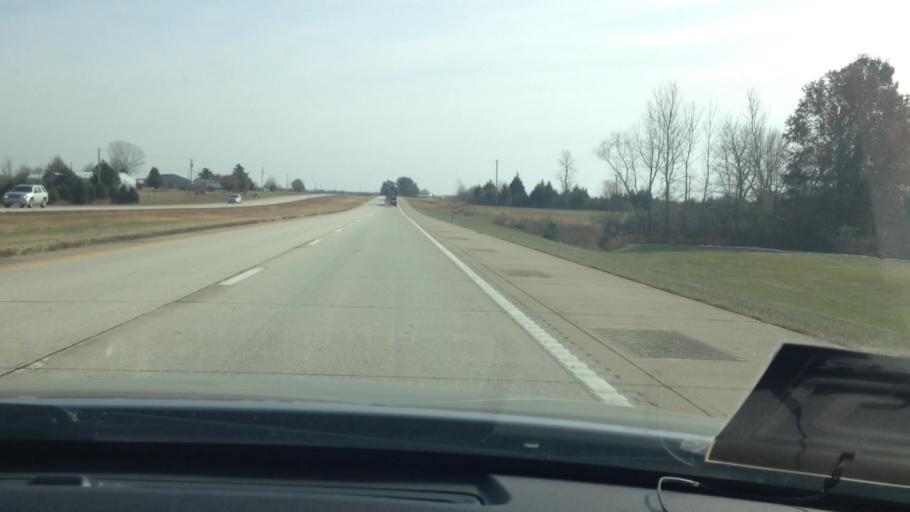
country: US
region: Missouri
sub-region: Henry County
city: Clinton
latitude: 38.4325
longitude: -93.9307
